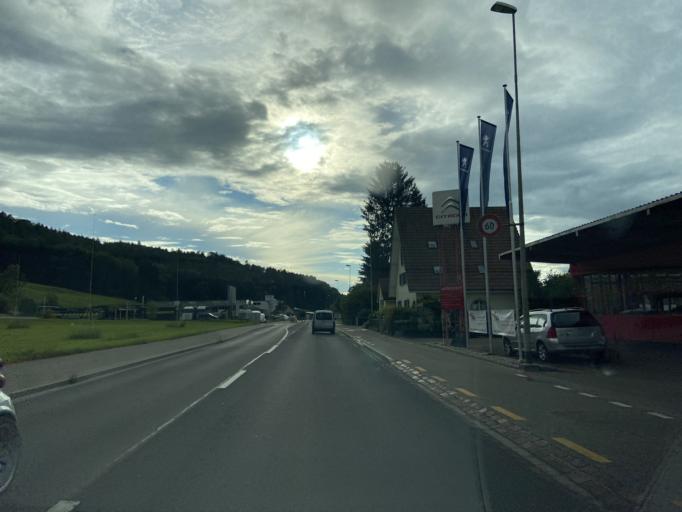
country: CH
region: Zurich
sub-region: Bezirk Winterthur
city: Elsau-Raeterschen / Raeterschen
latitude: 47.4989
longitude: 8.7929
